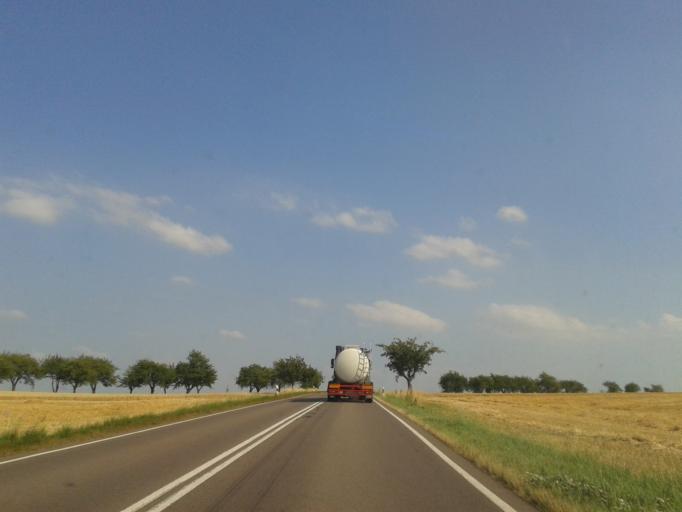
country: DE
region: Saxony
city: Wilsdruff
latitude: 51.0424
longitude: 13.5671
